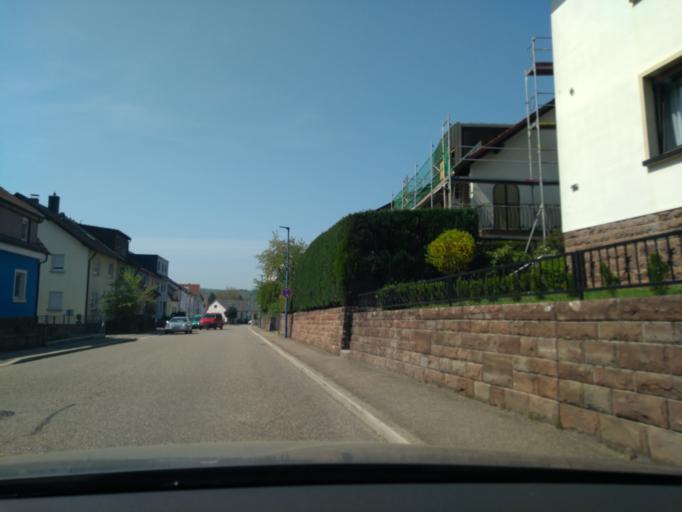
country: DE
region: Baden-Wuerttemberg
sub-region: Karlsruhe Region
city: Ettlingen
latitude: 48.9213
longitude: 8.4783
